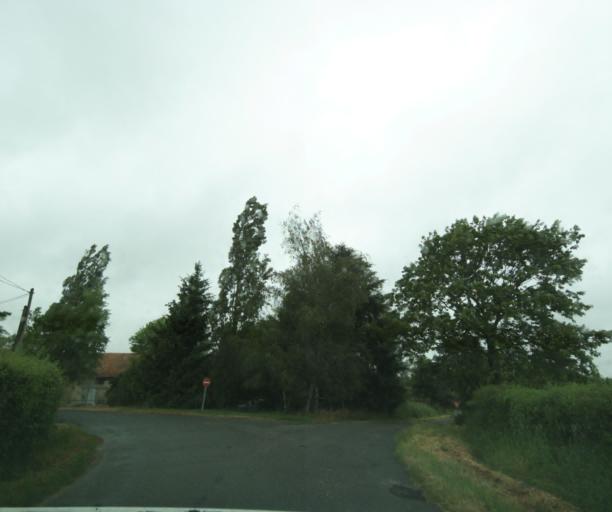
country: FR
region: Bourgogne
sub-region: Departement de Saone-et-Loire
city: Palinges
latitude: 46.5453
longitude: 4.1949
